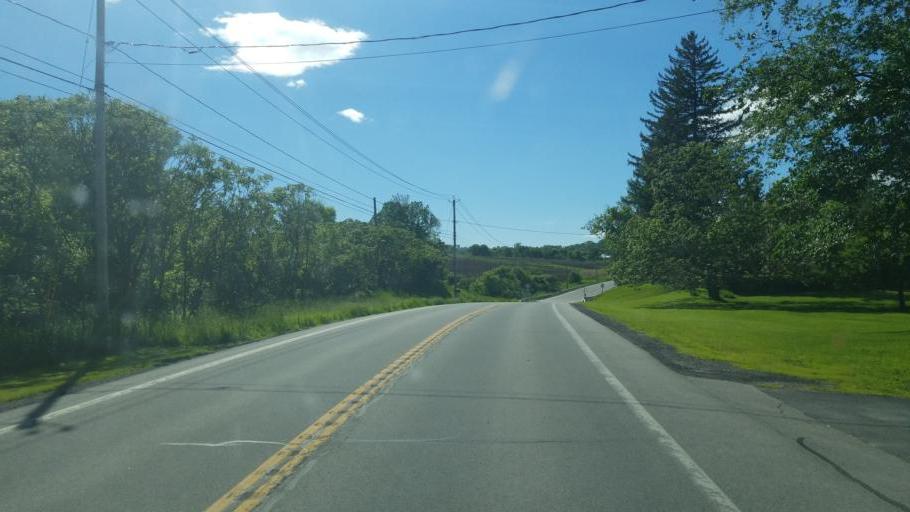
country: US
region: New York
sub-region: Montgomery County
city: Fort Plain
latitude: 42.9446
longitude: -74.6342
